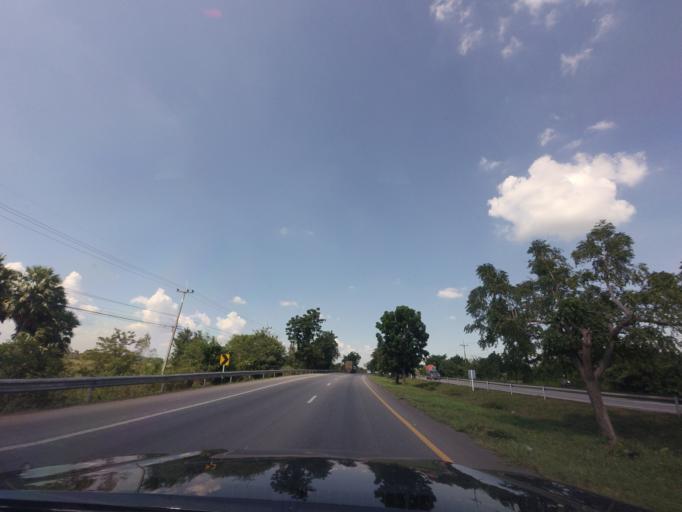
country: TH
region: Nakhon Ratchasima
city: Non Sung
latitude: 15.1375
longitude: 102.3114
